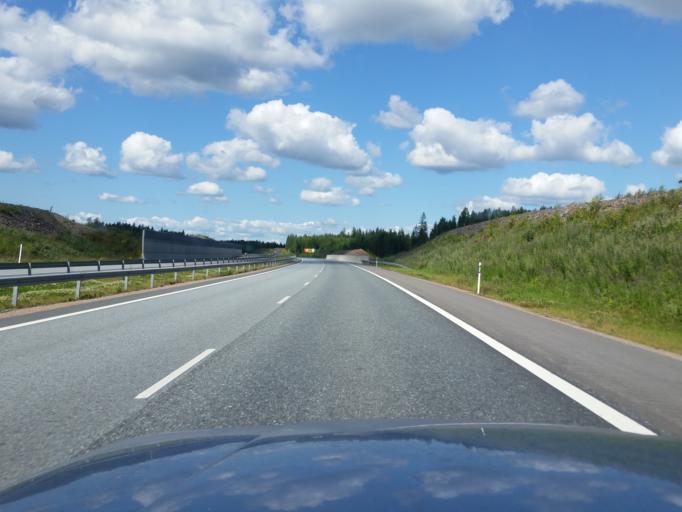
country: FI
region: Uusimaa
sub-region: Helsinki
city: Sammatti
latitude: 60.3646
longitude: 23.8788
